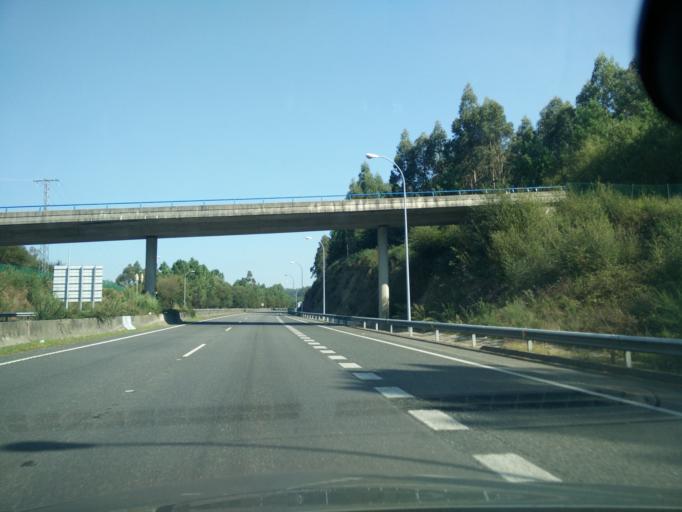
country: ES
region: Galicia
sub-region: Provincia da Coruna
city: Mino
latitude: 43.3769
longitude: -8.1833
